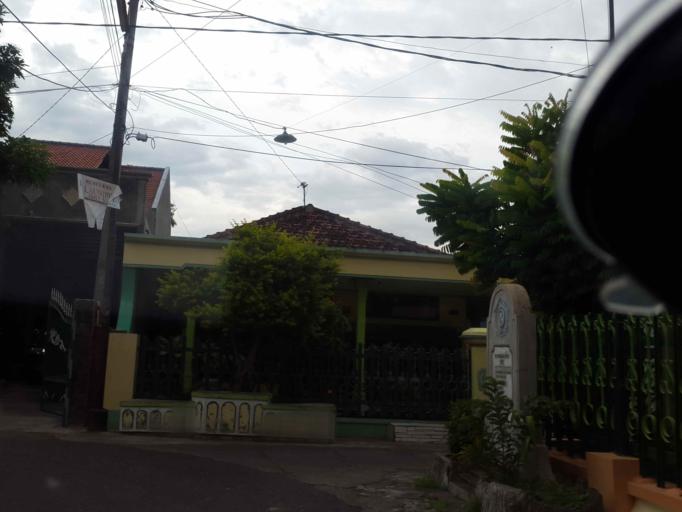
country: ID
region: East Java
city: Sumbergedong
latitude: -8.0534
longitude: 111.7099
